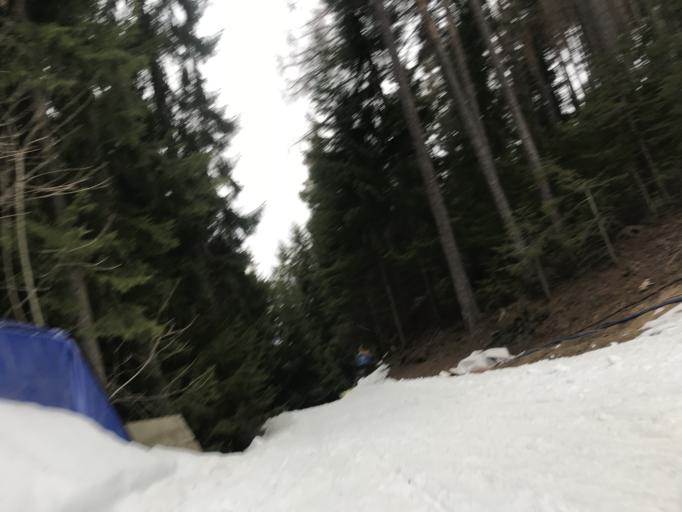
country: IT
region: Trentino-Alto Adige
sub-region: Bolzano
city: Bressanone
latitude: 46.6928
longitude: 11.6877
